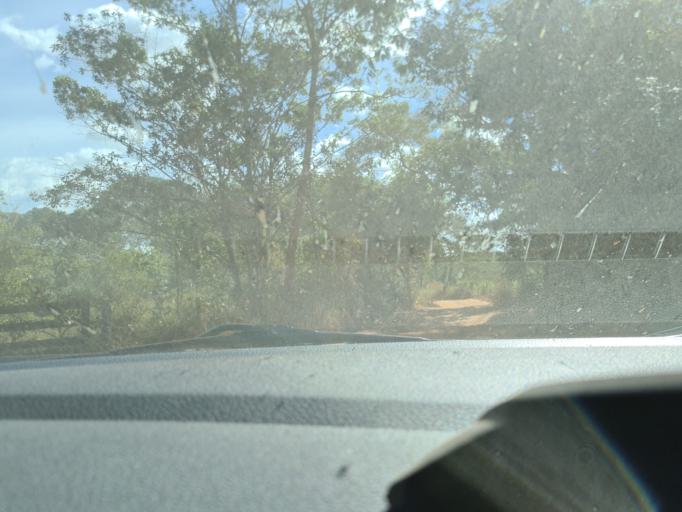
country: BR
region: Goias
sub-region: Silvania
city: Silvania
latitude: -16.5360
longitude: -48.5846
